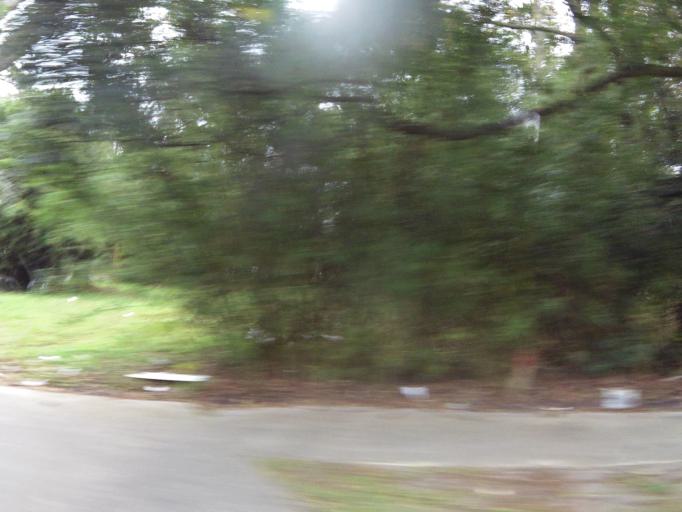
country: US
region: Florida
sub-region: Duval County
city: Jacksonville
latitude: 30.3679
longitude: -81.6989
